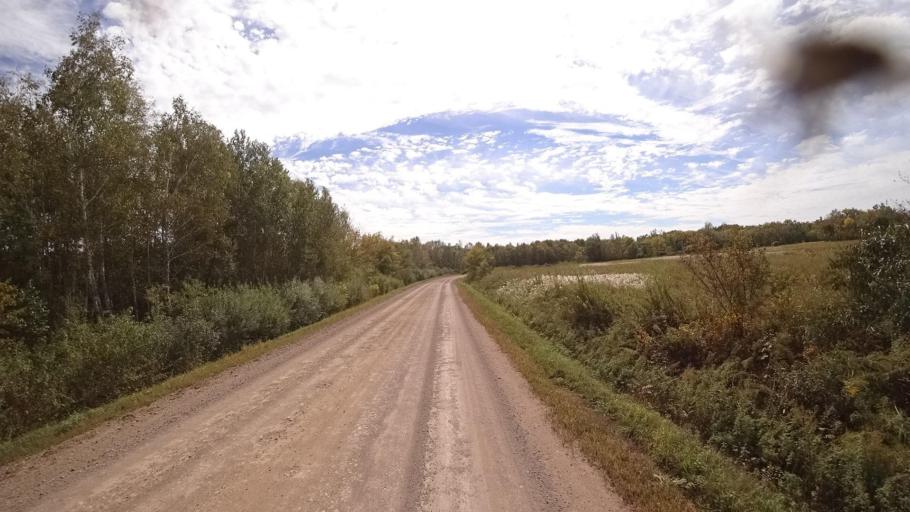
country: RU
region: Primorskiy
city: Yakovlevka
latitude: 44.5356
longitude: 133.6051
